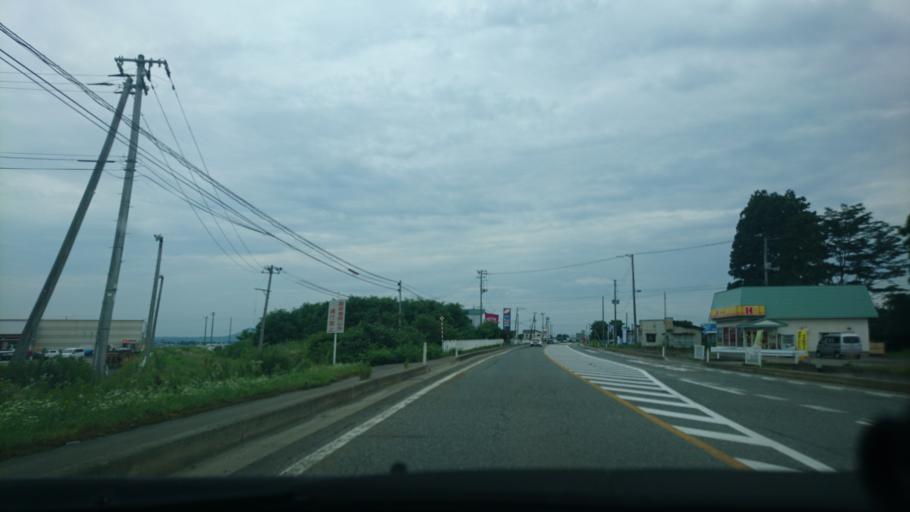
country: JP
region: Akita
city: Omagari
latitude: 39.4169
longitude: 140.5428
